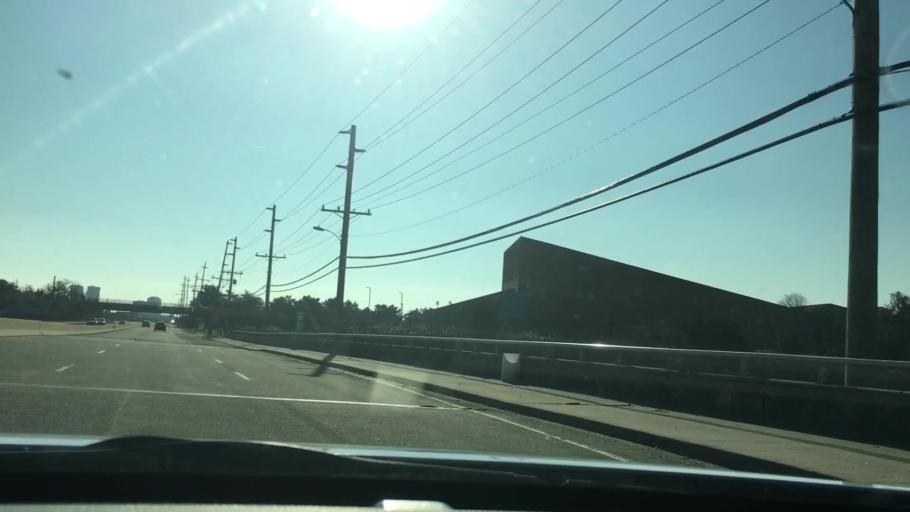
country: US
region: New Jersey
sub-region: Atlantic County
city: Ventnor City
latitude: 39.3700
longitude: -74.4764
